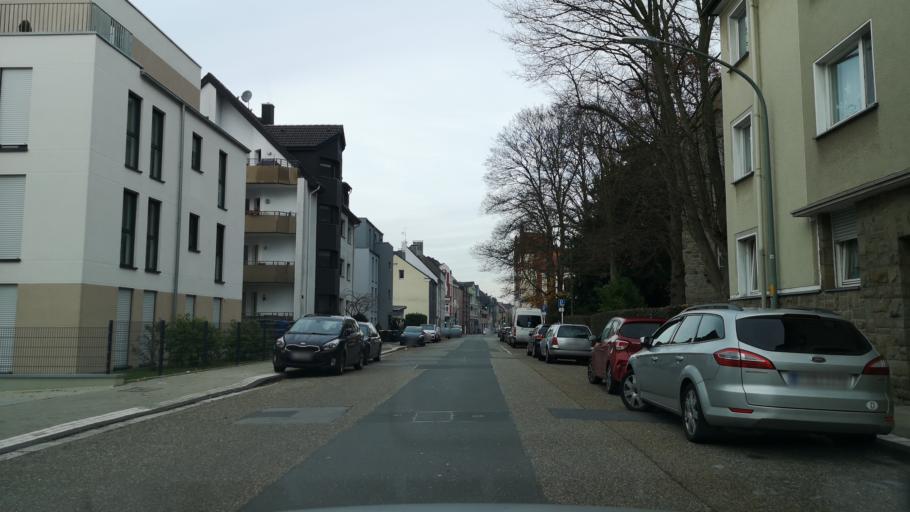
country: DE
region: North Rhine-Westphalia
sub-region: Regierungsbezirk Dusseldorf
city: Velbert
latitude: 51.3848
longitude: 7.0870
